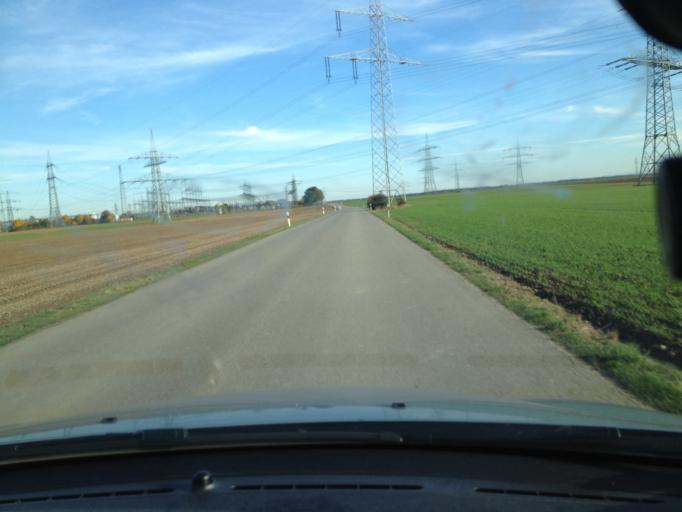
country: DE
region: Bavaria
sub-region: Swabia
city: Oberottmarshausen
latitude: 48.2388
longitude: 10.8317
